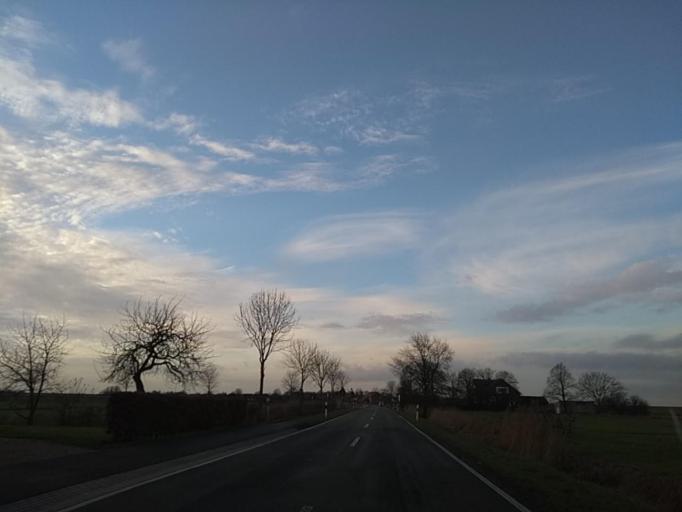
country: DE
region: Lower Saxony
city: Jemgum
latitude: 53.3108
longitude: 7.2966
